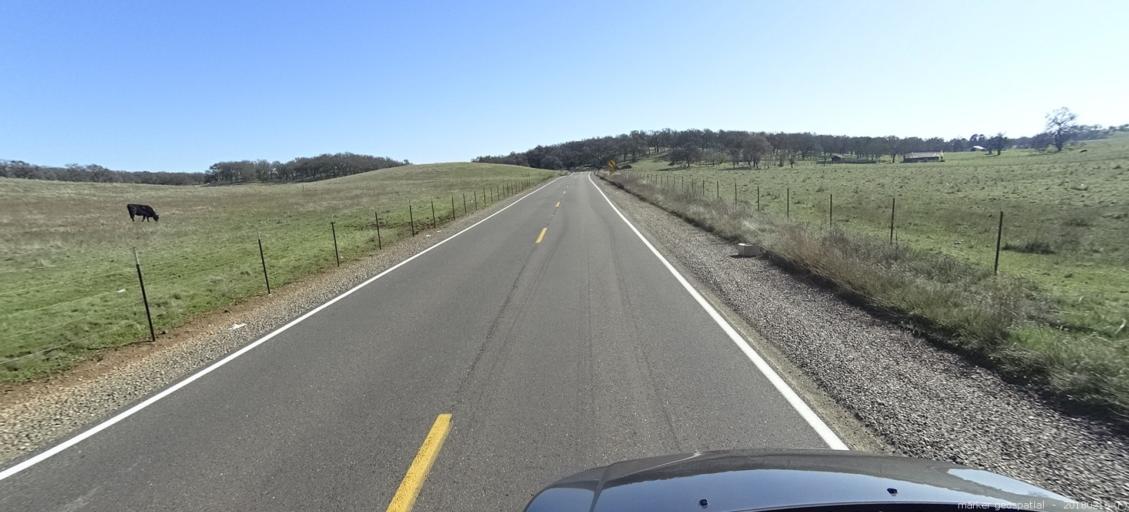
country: US
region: California
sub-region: Sacramento County
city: Rancho Murieta
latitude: 38.5463
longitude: -121.1113
